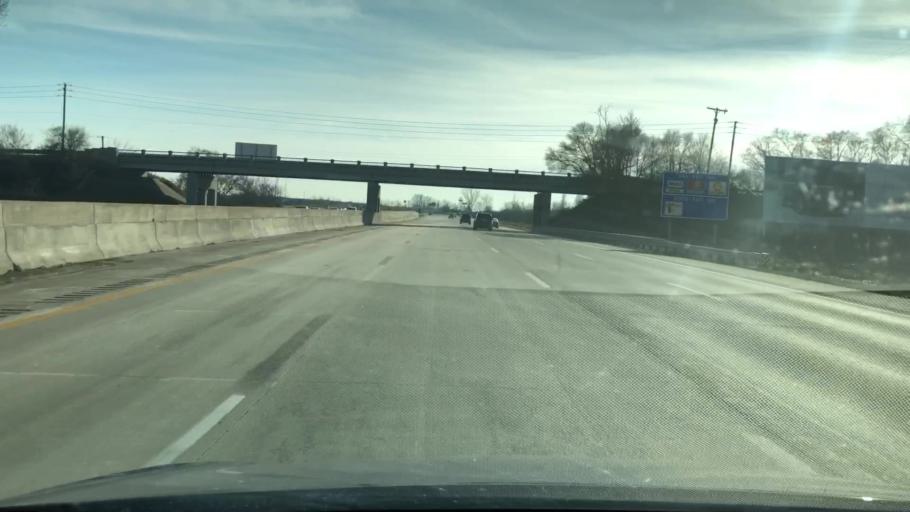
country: US
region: Michigan
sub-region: Bay County
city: Bay City
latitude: 43.5670
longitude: -83.9495
